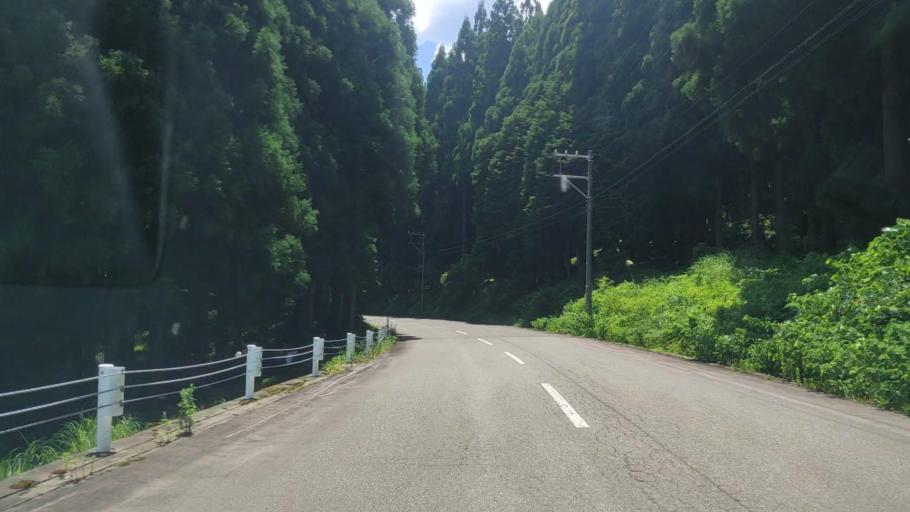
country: JP
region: Fukui
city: Ono
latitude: 35.8819
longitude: 136.5050
